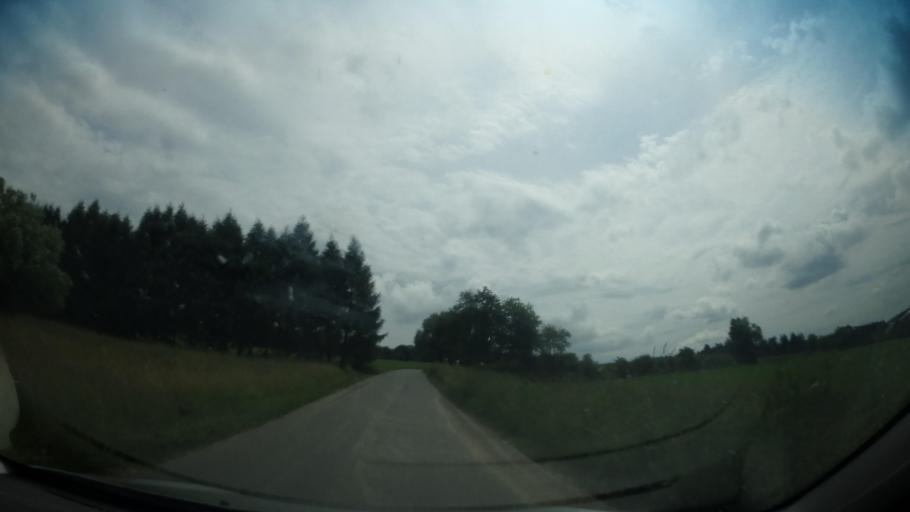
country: CZ
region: Vysocina
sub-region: Okres Zd'ar nad Sazavou
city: Nove Mesto na Morave
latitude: 49.6018
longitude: 16.0551
